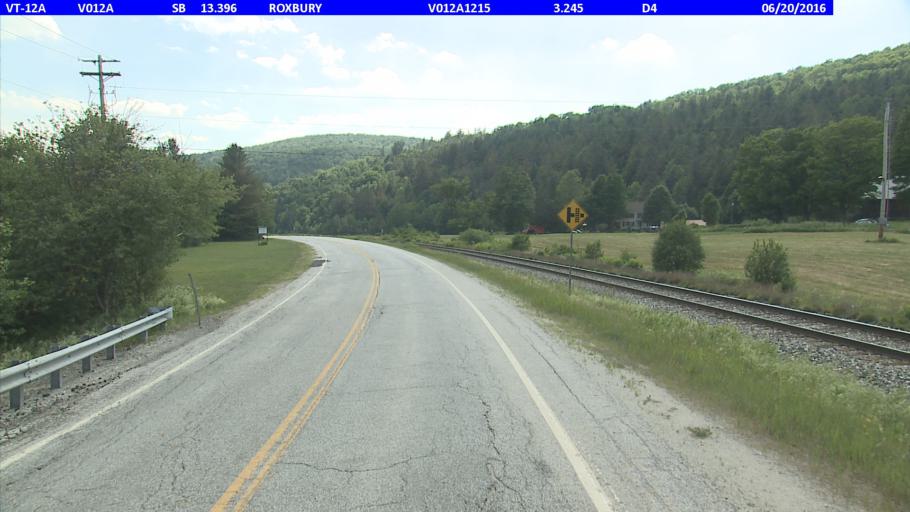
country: US
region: Vermont
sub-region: Washington County
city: Northfield
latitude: 44.0748
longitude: -72.7440
